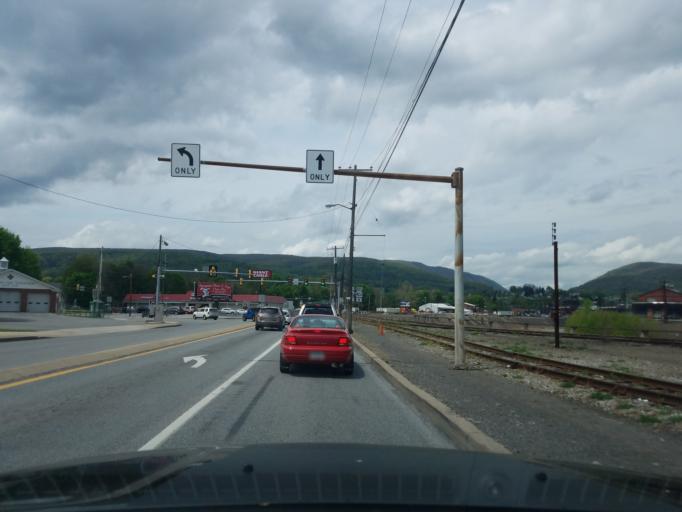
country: US
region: Pennsylvania
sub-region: Cambria County
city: Johnstown
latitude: 40.3445
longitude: -78.9378
